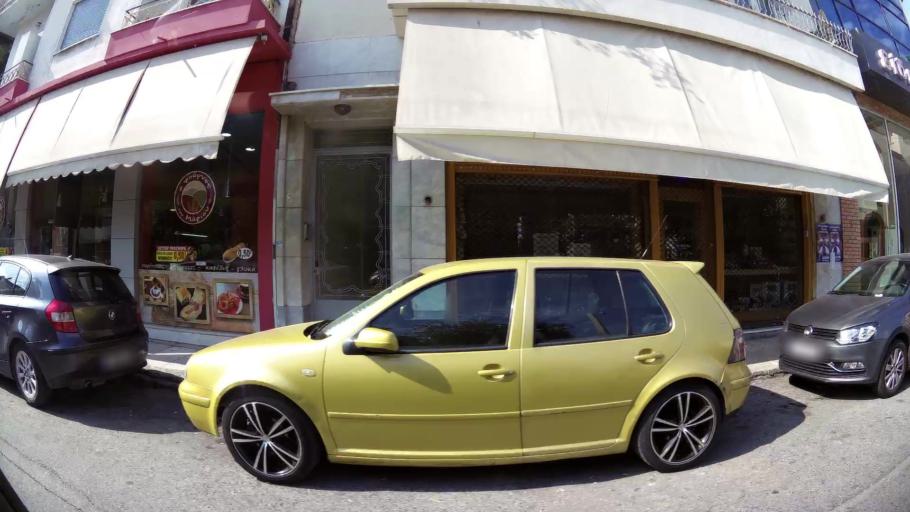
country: GR
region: Attica
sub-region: Nomarchia Athinas
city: Kipseli
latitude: 38.0016
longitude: 23.7190
